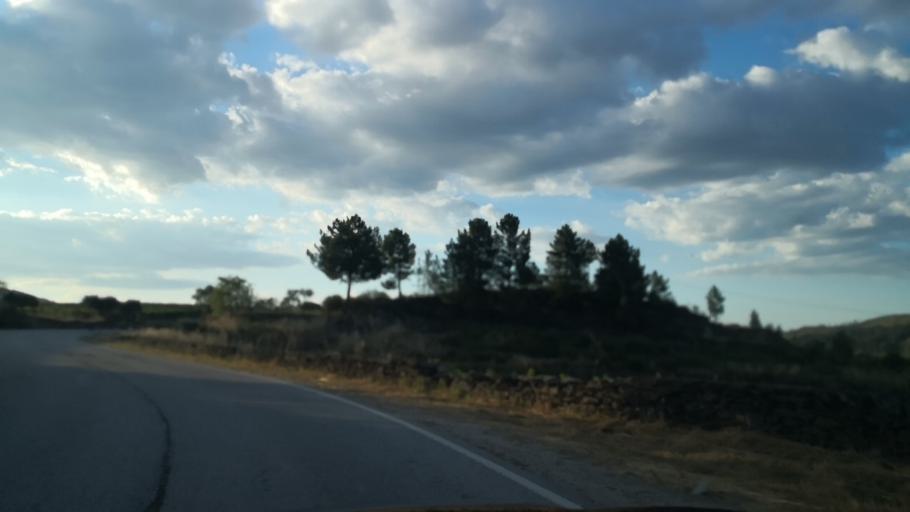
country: PT
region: Vila Real
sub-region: Sabrosa
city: Sabrosa
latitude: 41.2686
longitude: -7.4557
